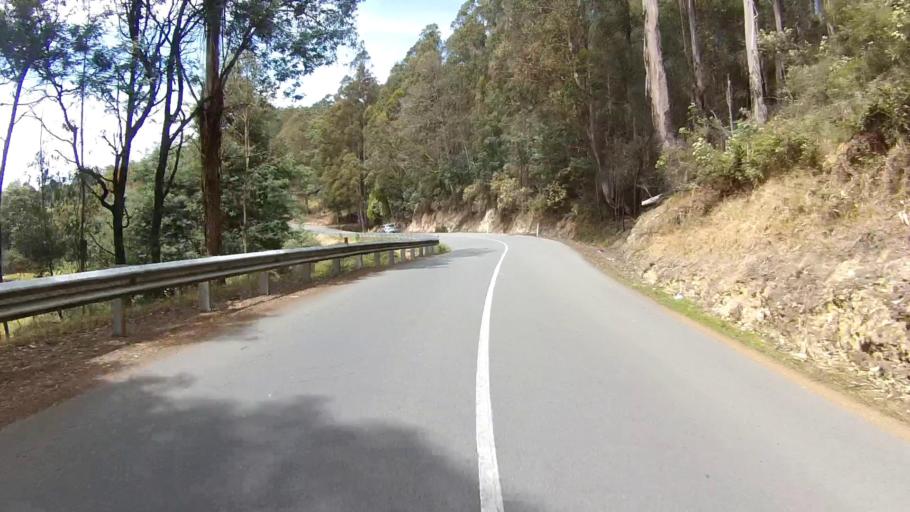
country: AU
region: Tasmania
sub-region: Kingborough
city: Kettering
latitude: -43.1038
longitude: 147.2162
